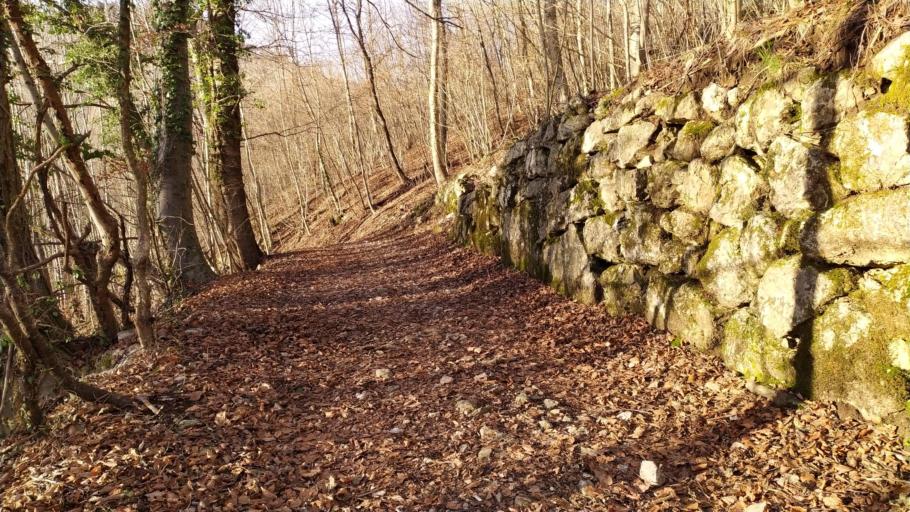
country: IT
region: Veneto
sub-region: Provincia di Vicenza
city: Velo d'Astico
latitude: 45.7677
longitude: 11.3548
